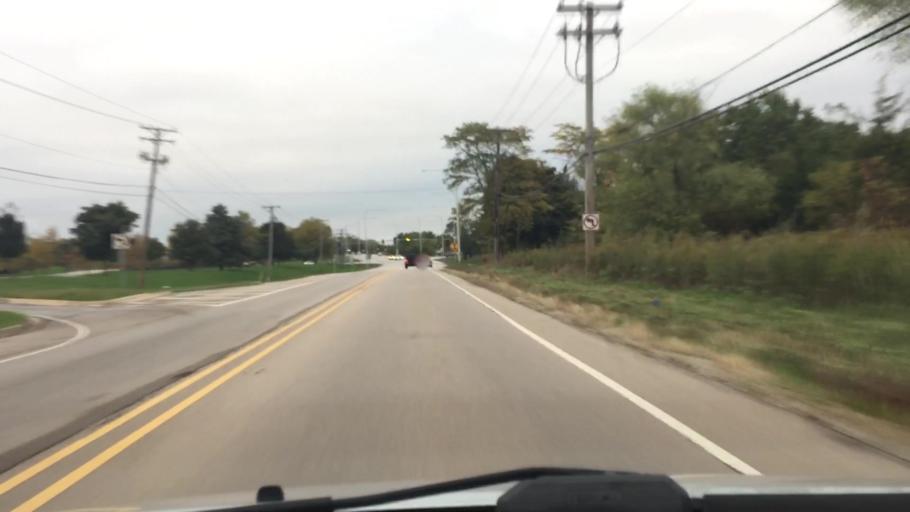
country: US
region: Illinois
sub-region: Kane County
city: Farmington
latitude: 41.9481
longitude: -88.3178
